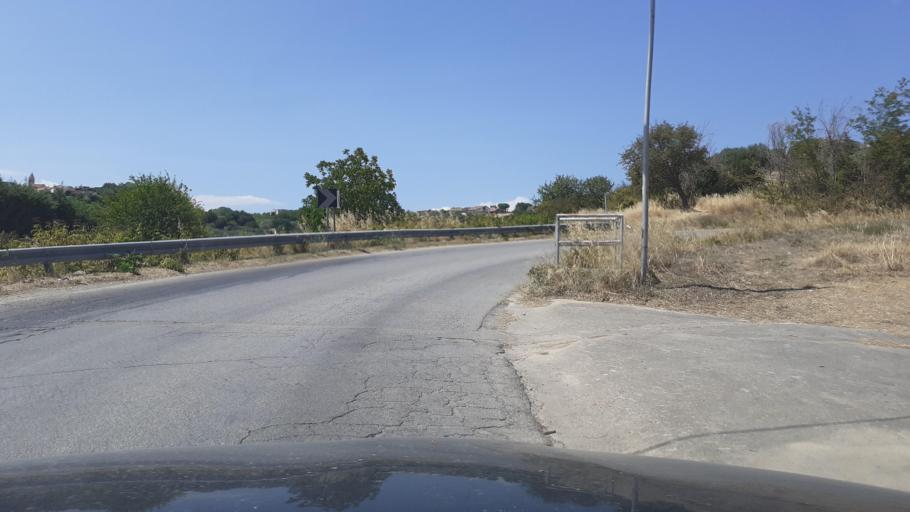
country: IT
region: Abruzzo
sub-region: Provincia di Chieti
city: Santa Maria Imbaro
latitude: 42.2148
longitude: 14.4543
